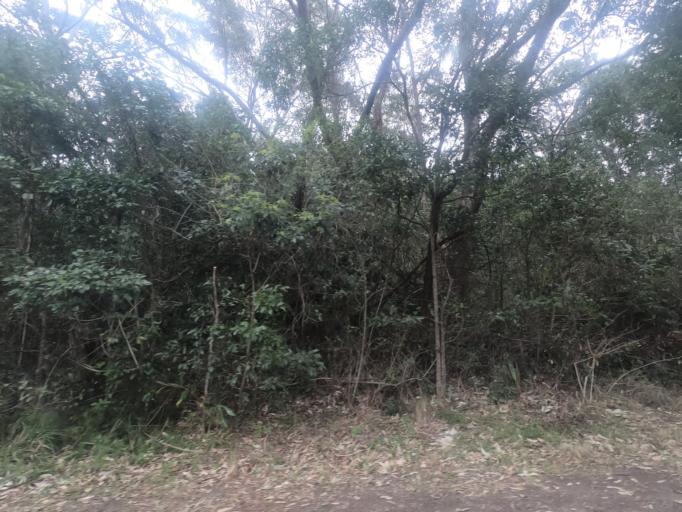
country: AU
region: New South Wales
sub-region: Wollongong
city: Bulli
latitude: -34.2931
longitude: 150.9357
